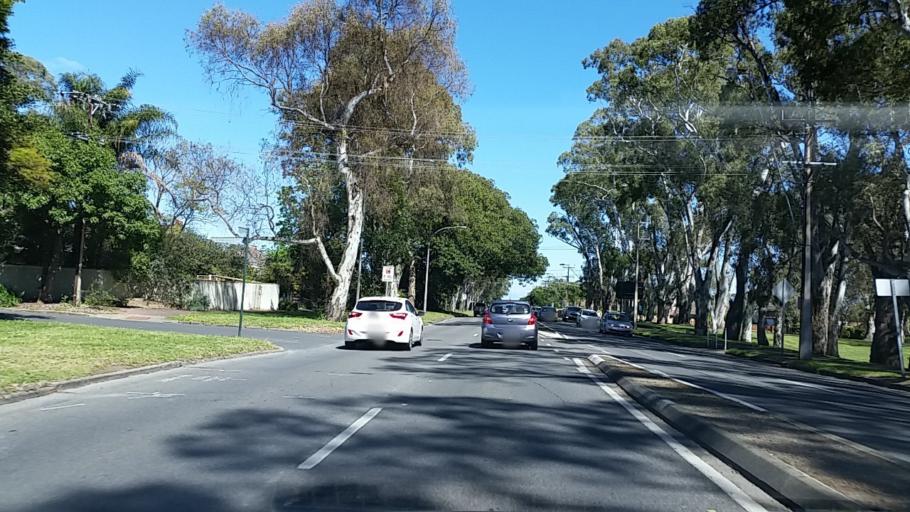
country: AU
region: South Australia
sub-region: Burnside
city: Hazelwood Park
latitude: -34.9384
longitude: 138.6580
